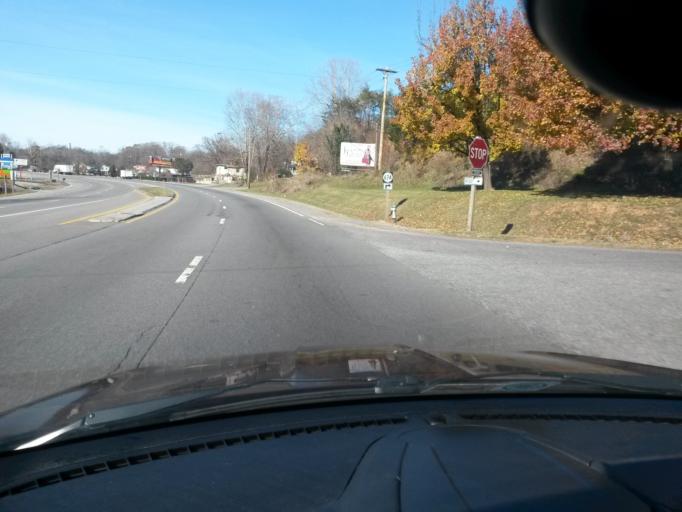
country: US
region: Virginia
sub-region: Roanoke County
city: Narrows
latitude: 37.1979
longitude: -79.9431
